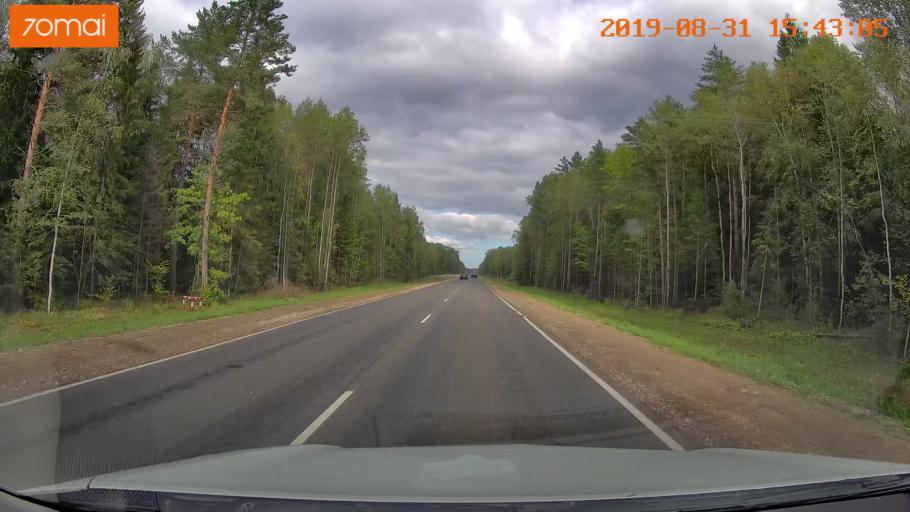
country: RU
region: Kaluga
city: Mosal'sk
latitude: 54.6506
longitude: 34.9022
